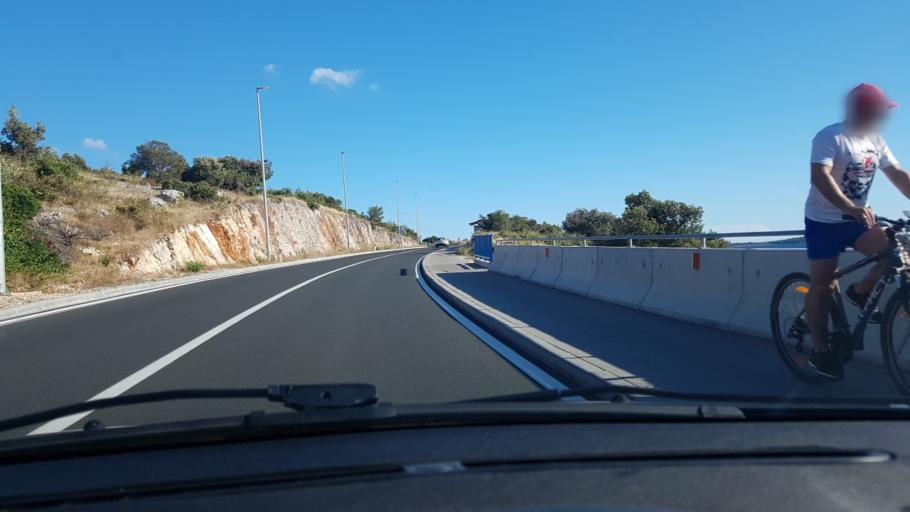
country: HR
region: Sibensko-Kniniska
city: Primosten
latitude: 43.6031
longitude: 15.9222
